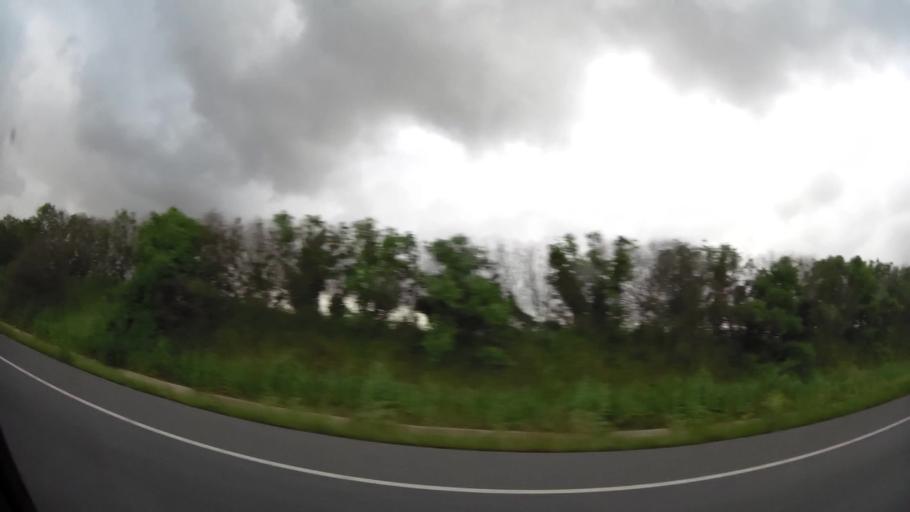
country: MA
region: Grand Casablanca
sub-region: Mediouna
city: Tit Mellil
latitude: 33.5935
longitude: -7.4470
